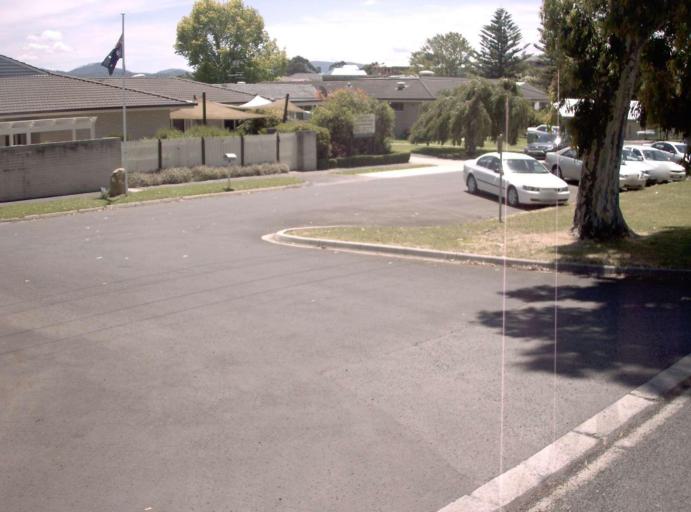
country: AU
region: Victoria
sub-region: Baw Baw
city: Warragul
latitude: -38.0223
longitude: 145.9545
